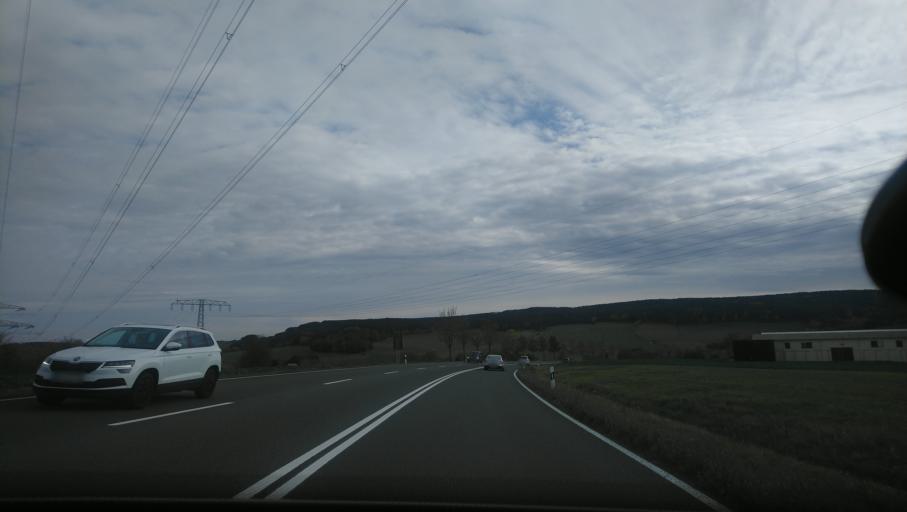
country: DE
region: Saxony
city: Dorfchemnitz
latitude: 50.6518
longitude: 12.8196
